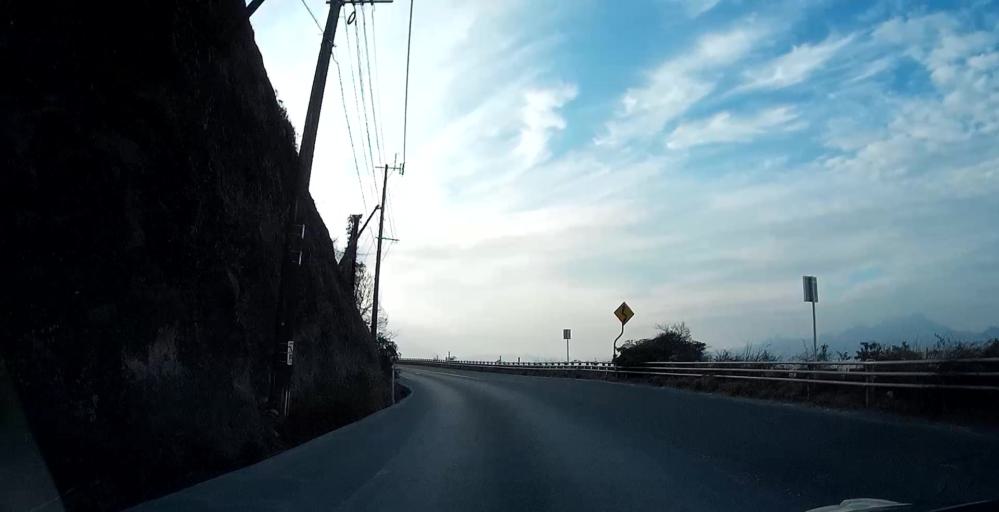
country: JP
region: Nagasaki
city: Shimabara
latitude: 32.6351
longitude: 130.4644
